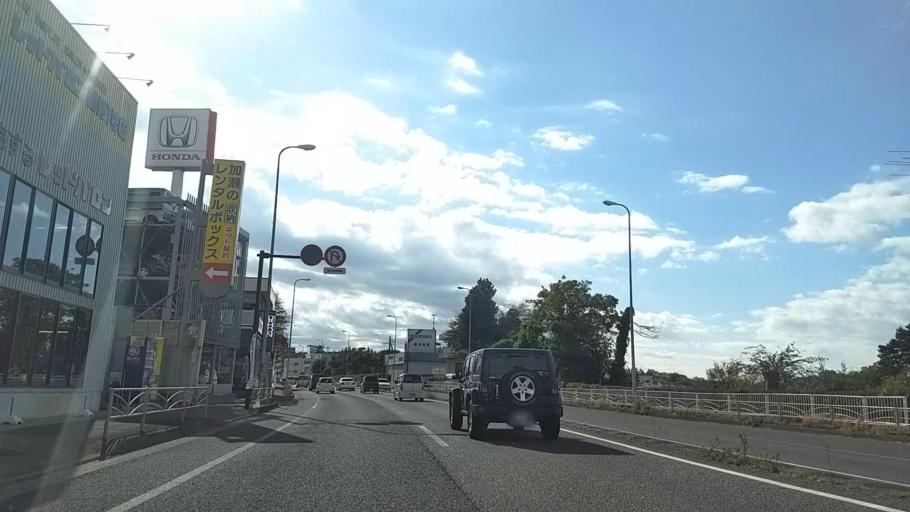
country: JP
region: Kanagawa
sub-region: Kawasaki-shi
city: Kawasaki
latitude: 35.5083
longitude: 139.6620
